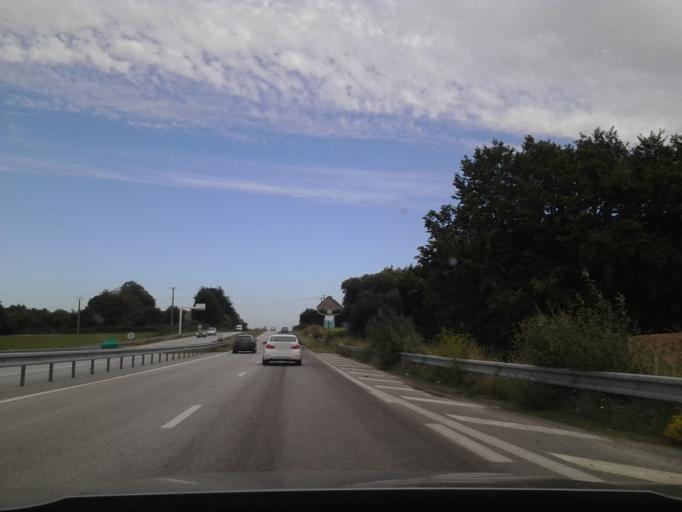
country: FR
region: Lower Normandy
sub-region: Departement de la Manche
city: La Glacerie
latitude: 49.5851
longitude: -1.5941
